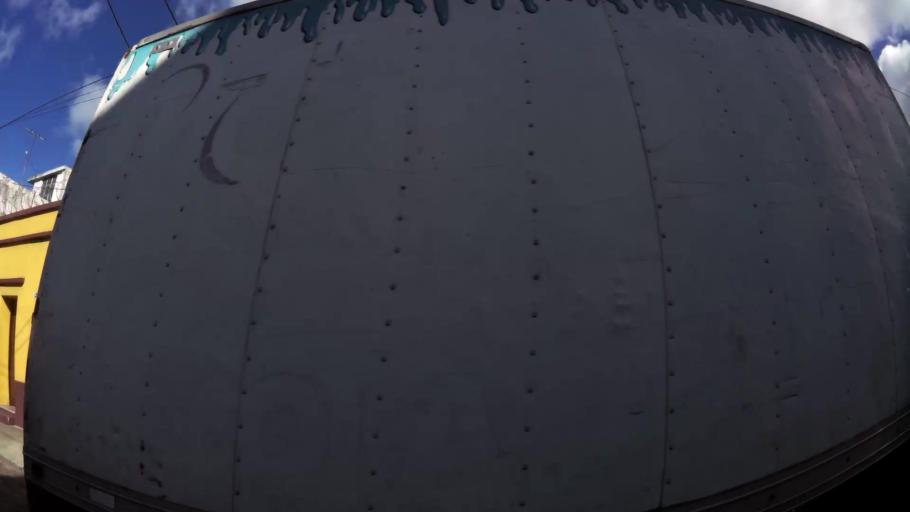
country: GT
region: Guatemala
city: Guatemala City
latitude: 14.6202
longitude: -90.5013
